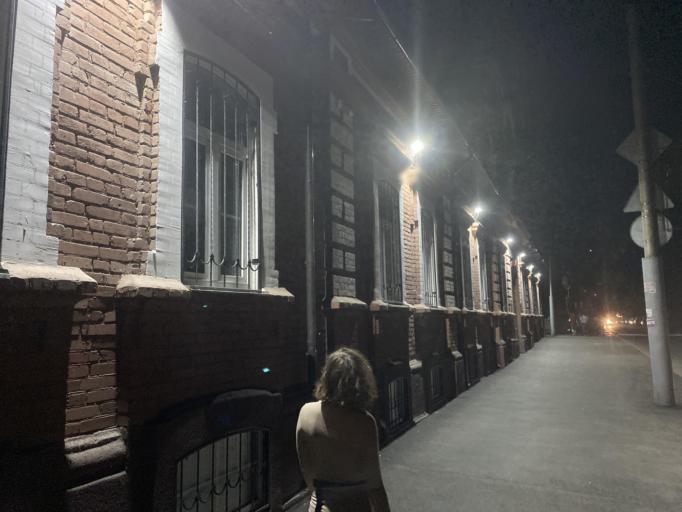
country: RU
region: Saratov
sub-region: Saratovskiy Rayon
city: Saratov
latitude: 51.5263
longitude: 46.0496
